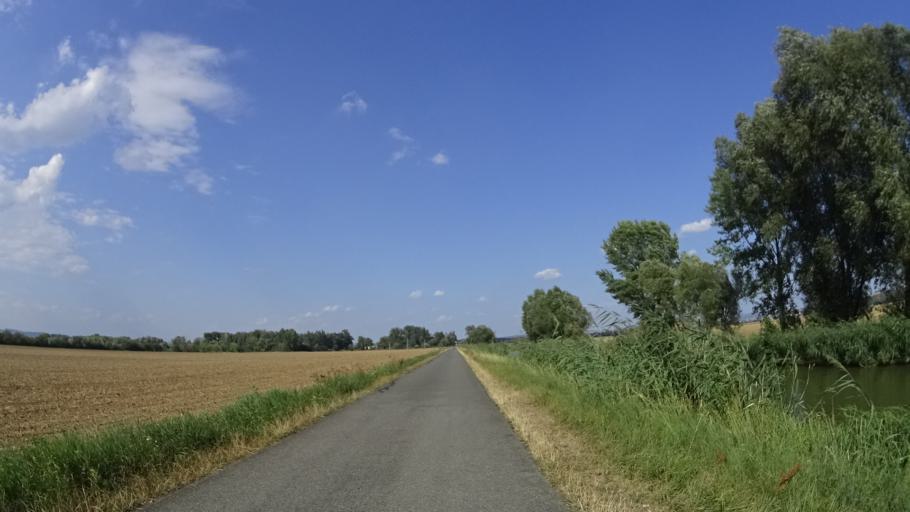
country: CZ
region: Zlin
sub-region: Okres Uherske Hradiste
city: Uherske Hradiste
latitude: 49.0794
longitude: 17.4606
